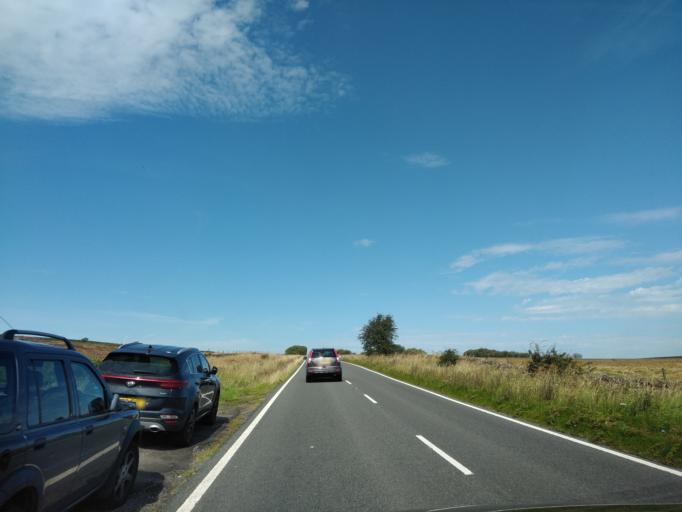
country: GB
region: England
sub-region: Derbyshire
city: Hathersage
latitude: 53.3010
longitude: -1.5881
